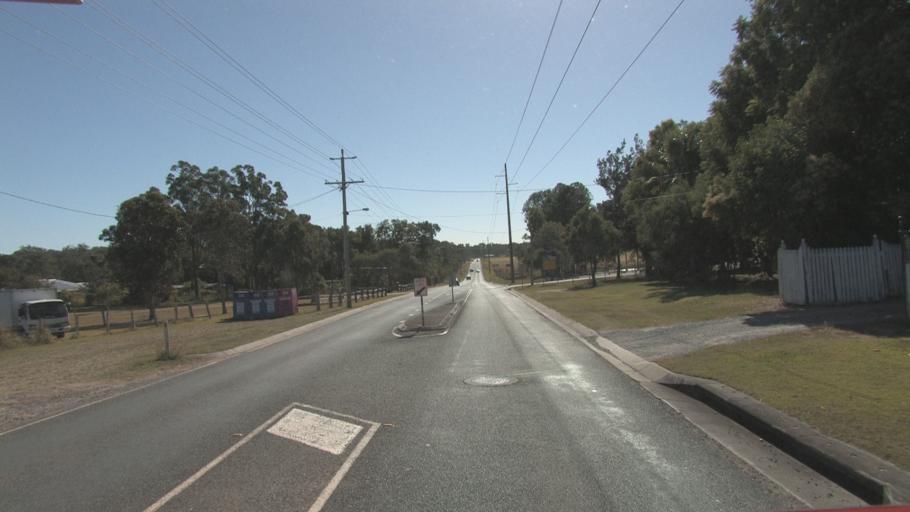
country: AU
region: Queensland
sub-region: Logan
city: Chambers Flat
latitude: -27.7587
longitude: 153.0912
